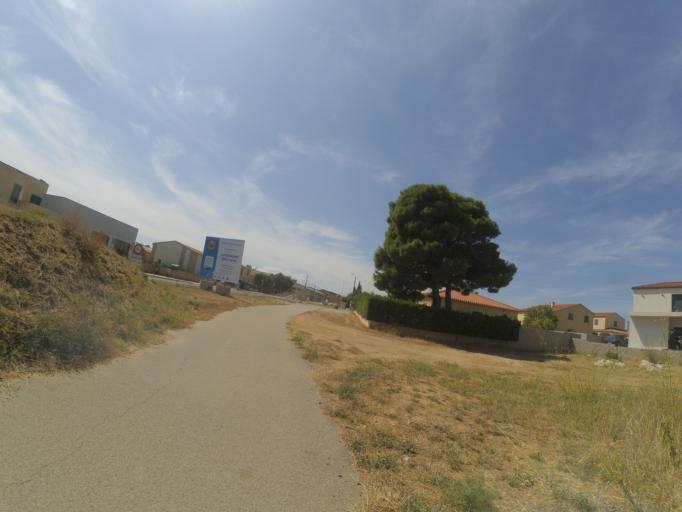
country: FR
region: Languedoc-Roussillon
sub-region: Departement des Pyrenees-Orientales
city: Baixas
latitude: 42.7534
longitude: 2.8183
